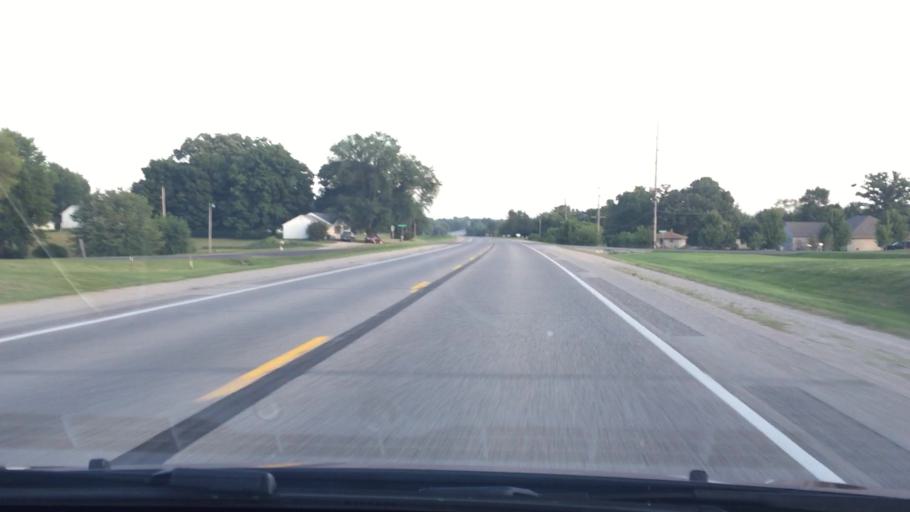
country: US
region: Iowa
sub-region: Muscatine County
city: Muscatine
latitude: 41.4711
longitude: -91.0369
